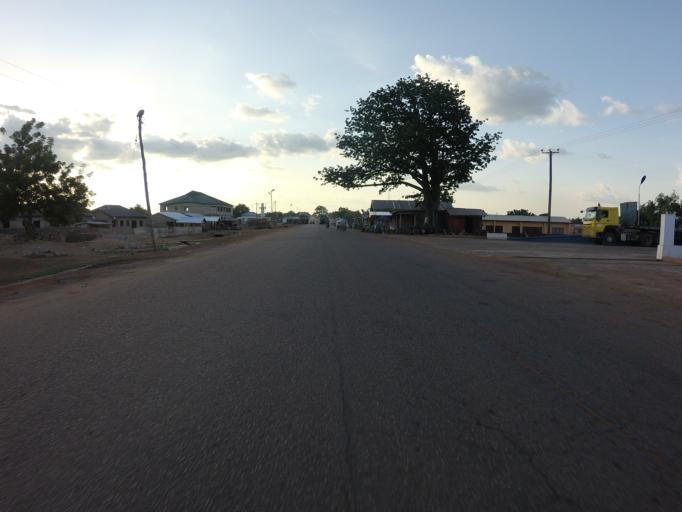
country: GH
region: Upper East
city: Navrongo
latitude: 10.9902
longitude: -1.1105
